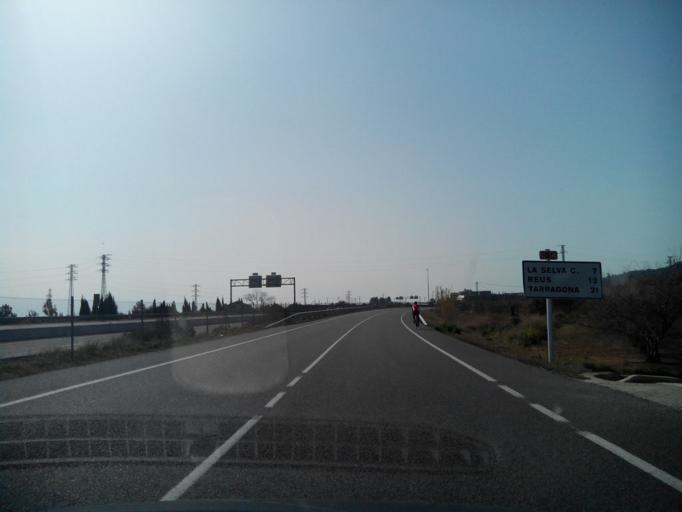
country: ES
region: Catalonia
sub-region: Provincia de Tarragona
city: Alcover
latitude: 41.2575
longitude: 1.1751
